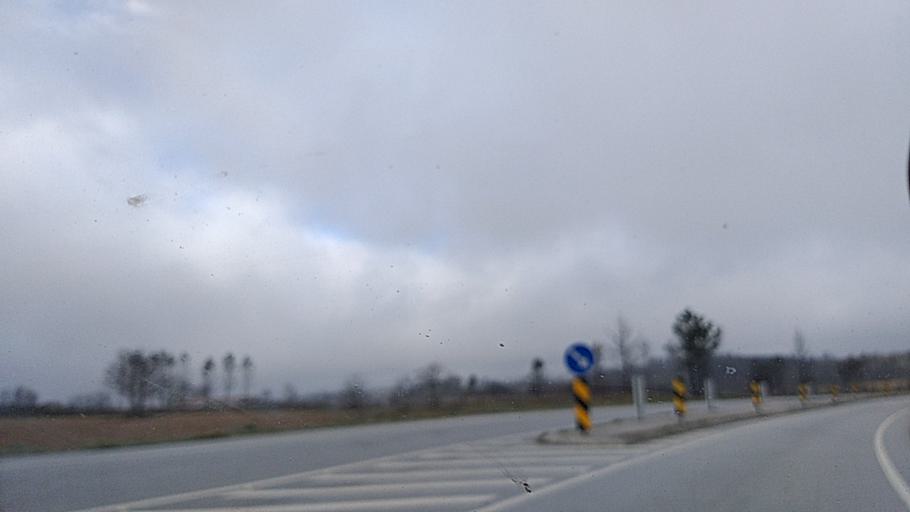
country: PT
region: Guarda
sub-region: Fornos de Algodres
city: Fornos de Algodres
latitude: 40.6931
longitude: -7.4728
